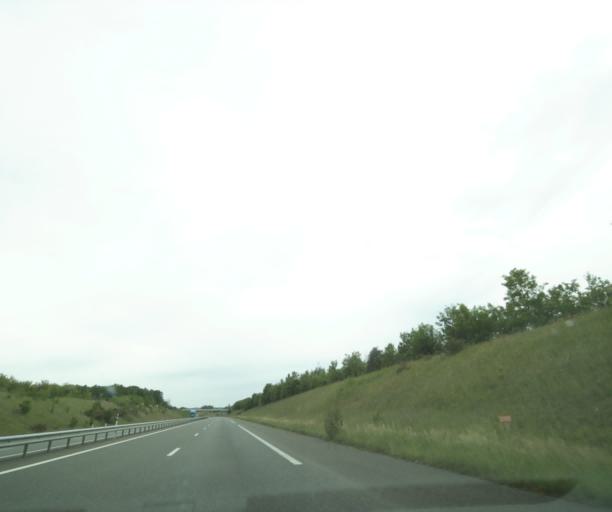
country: FR
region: Midi-Pyrenees
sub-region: Departement du Tarn-et-Garonne
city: Caussade
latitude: 44.2162
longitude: 1.5402
